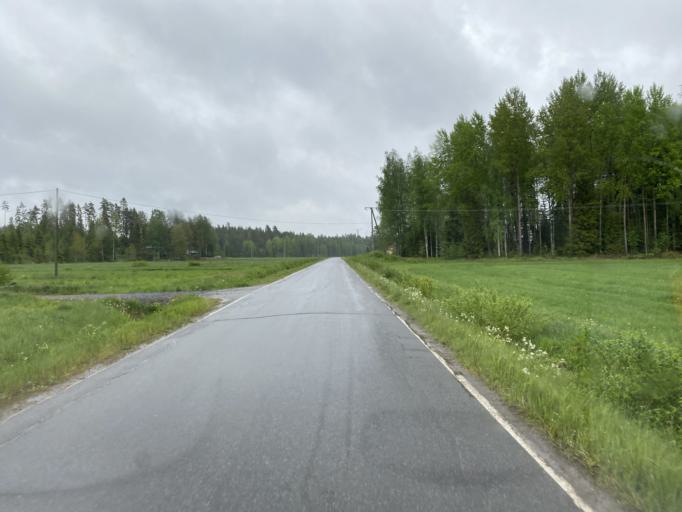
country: FI
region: Haeme
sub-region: Forssa
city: Humppila
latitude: 61.0503
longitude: 23.3550
